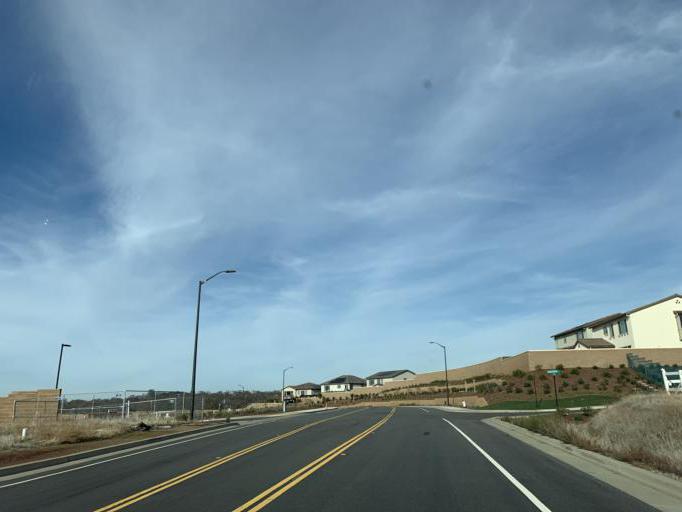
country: US
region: California
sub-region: El Dorado County
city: Cameron Park
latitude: 38.6744
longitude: -121.0264
